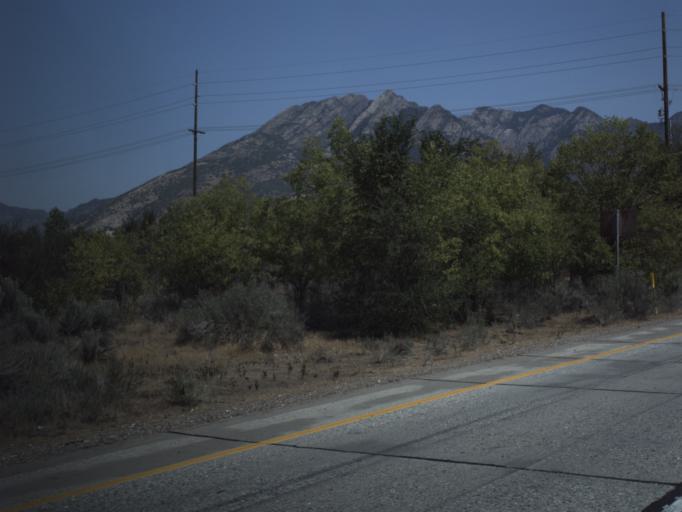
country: US
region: Utah
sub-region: Salt Lake County
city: Cottonwood Heights
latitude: 40.6318
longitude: -111.8354
